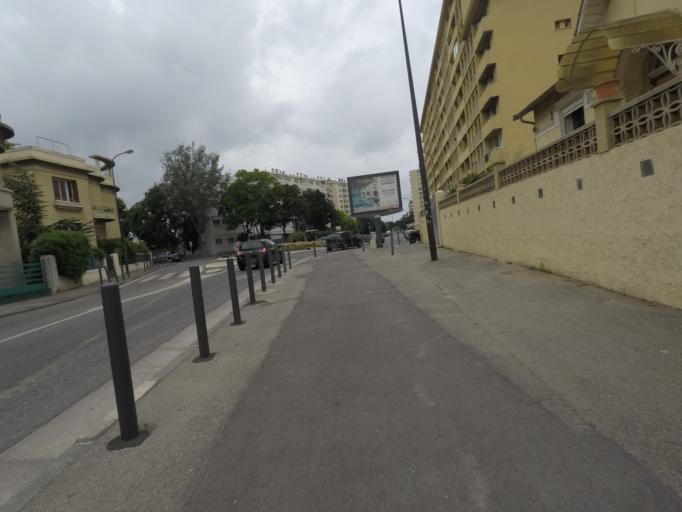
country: FR
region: Provence-Alpes-Cote d'Azur
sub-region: Departement des Bouches-du-Rhone
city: Marseille 09
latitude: 43.2680
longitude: 5.3995
